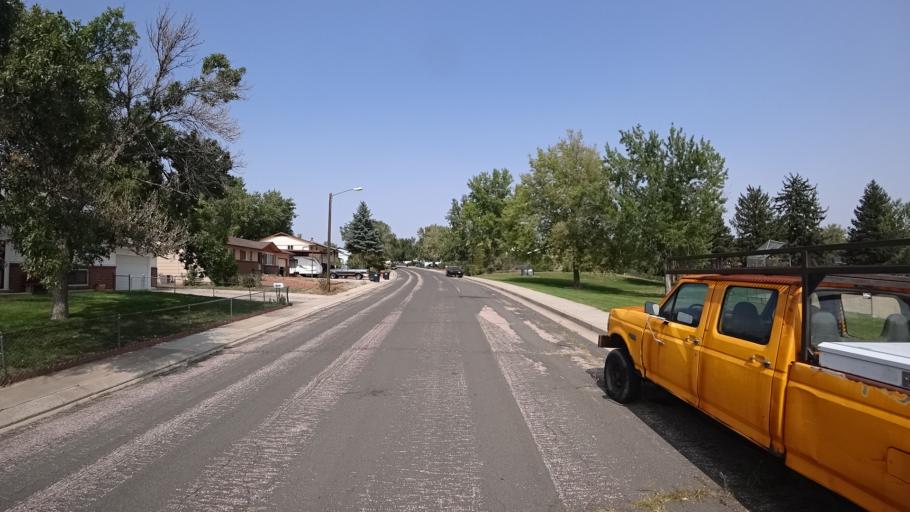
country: US
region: Colorado
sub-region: El Paso County
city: Stratmoor
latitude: 38.8012
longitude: -104.7681
